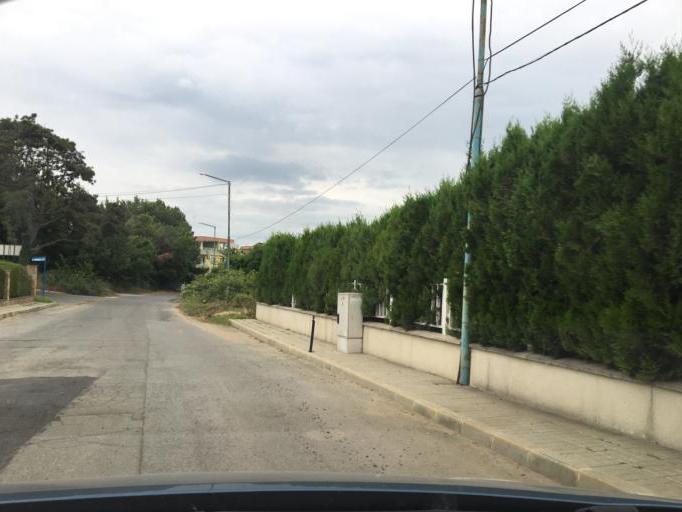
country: BG
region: Burgas
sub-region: Obshtina Sozopol
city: Sozopol
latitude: 42.4070
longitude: 27.7164
